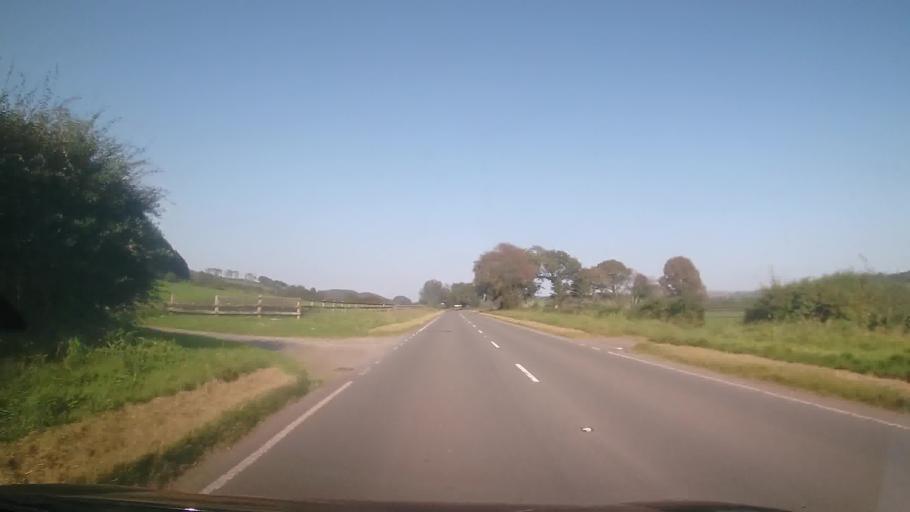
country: GB
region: Wales
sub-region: County of Ceredigion
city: Llangybi
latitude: 52.1636
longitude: -4.0290
